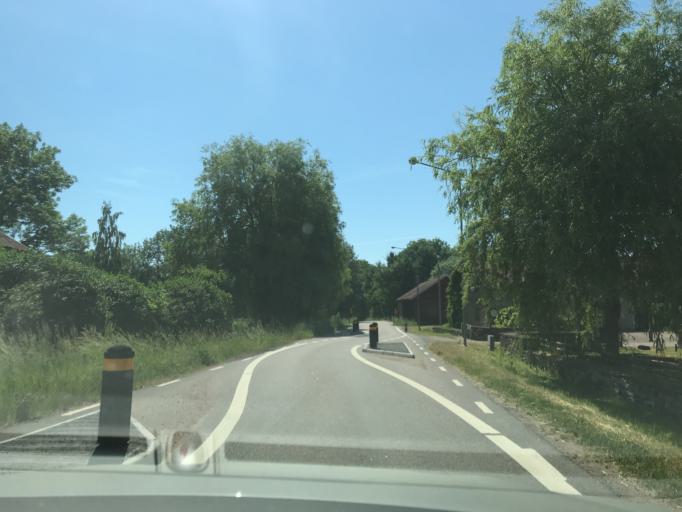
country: SE
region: Vaestra Goetaland
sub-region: Gotene Kommun
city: Kallby
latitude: 58.5581
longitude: 13.3489
